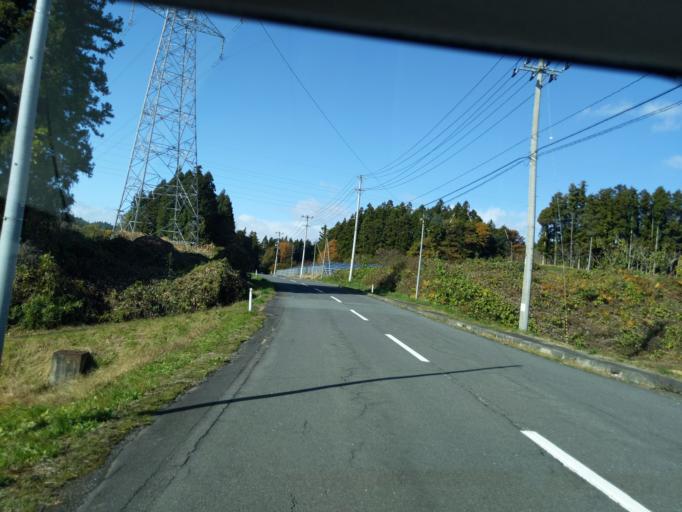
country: JP
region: Iwate
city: Mizusawa
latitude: 39.0258
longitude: 141.1095
